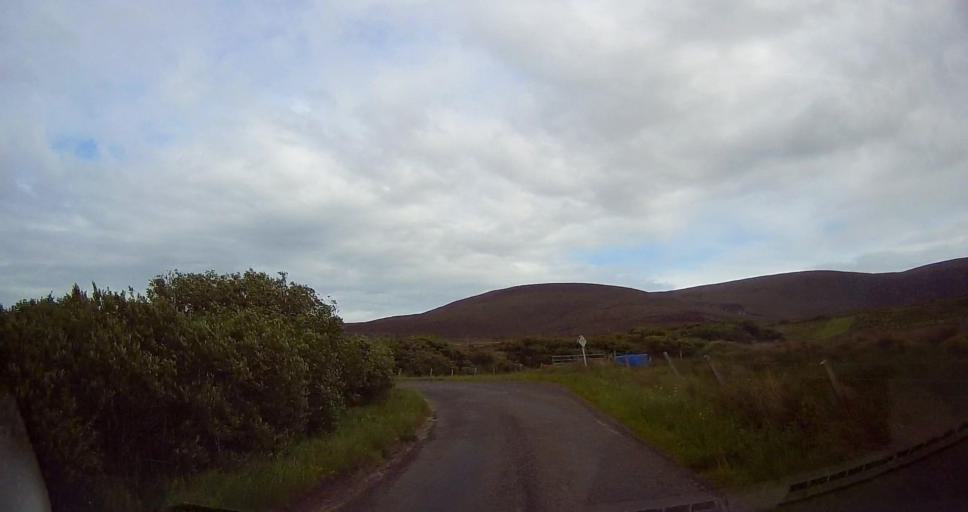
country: GB
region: Scotland
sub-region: Orkney Islands
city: Stromness
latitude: 58.9049
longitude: -3.3140
